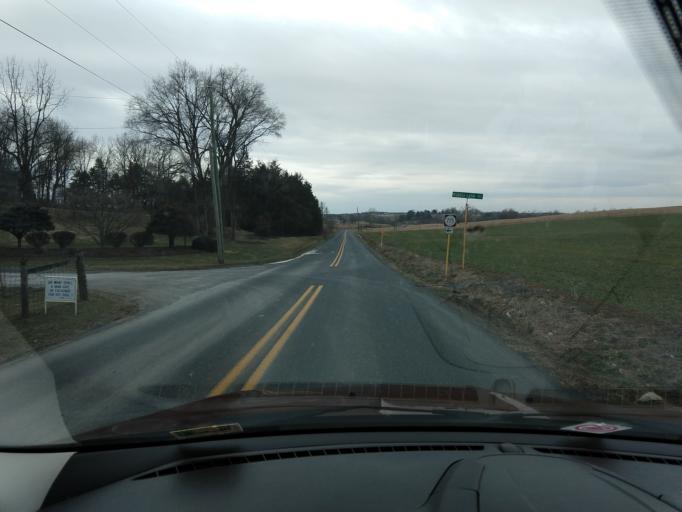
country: US
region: Virginia
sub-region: Augusta County
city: Weyers Cave
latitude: 38.2302
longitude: -78.8811
